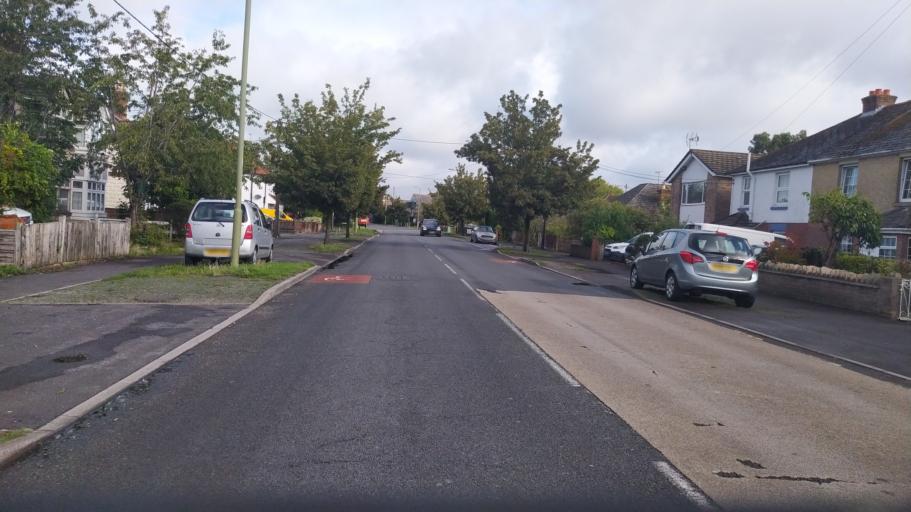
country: GB
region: England
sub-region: Hampshire
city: Totton
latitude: 50.9275
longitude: -1.5007
